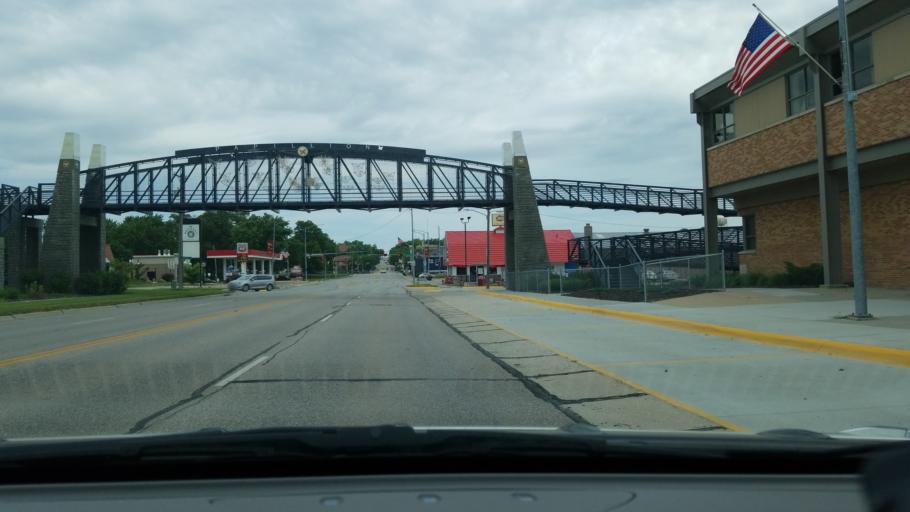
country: US
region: Nebraska
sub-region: Sarpy County
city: Papillion
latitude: 41.1529
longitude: -96.0429
